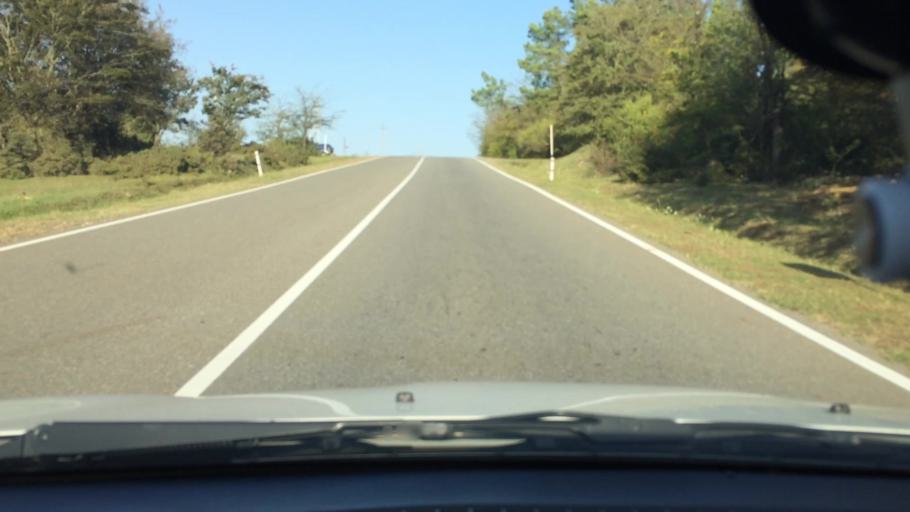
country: GE
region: Imereti
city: Kutaisi
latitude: 42.2513
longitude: 42.7520
